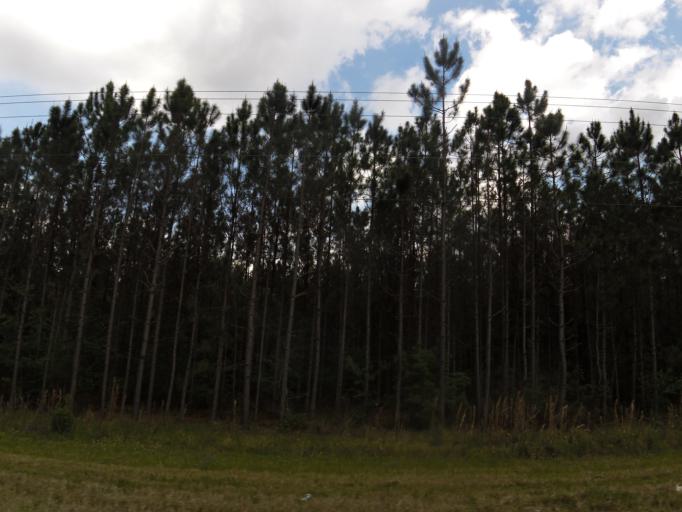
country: US
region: Georgia
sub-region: Charlton County
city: Folkston
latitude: 30.8509
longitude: -81.9311
